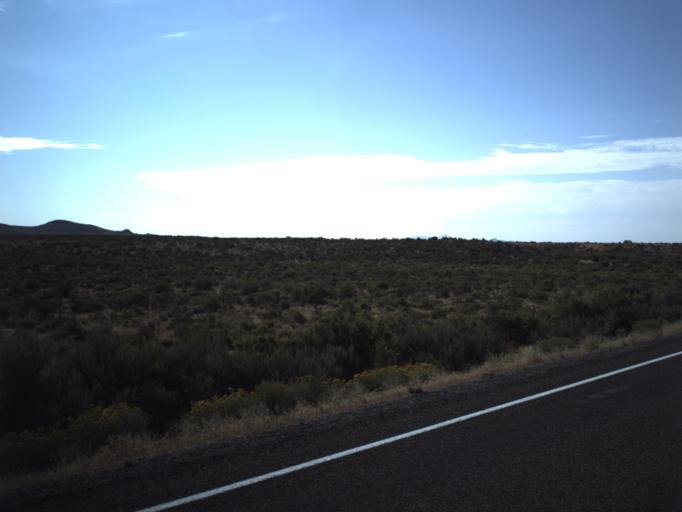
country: US
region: Idaho
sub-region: Cassia County
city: Burley
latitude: 41.6611
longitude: -113.5477
